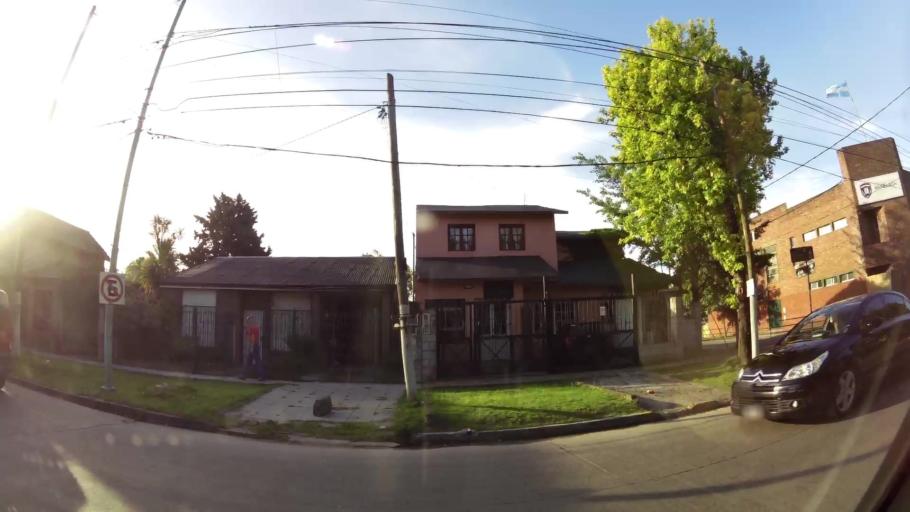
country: AR
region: Buenos Aires
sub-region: Partido de Quilmes
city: Quilmes
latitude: -34.7842
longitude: -58.2070
